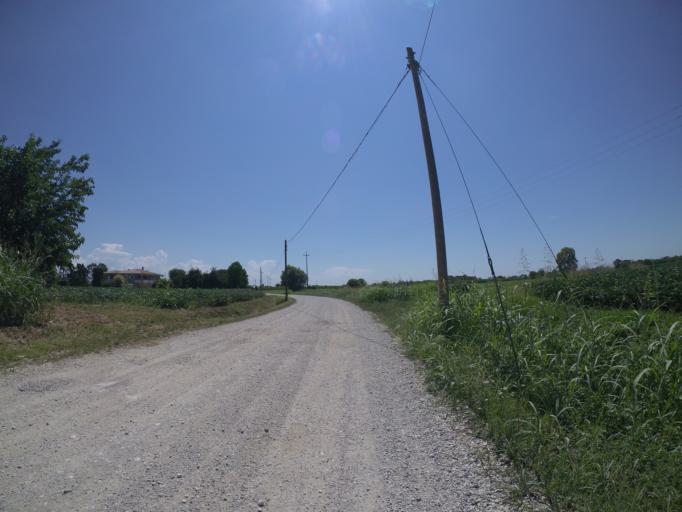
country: IT
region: Friuli Venezia Giulia
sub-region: Provincia di Udine
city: Talmassons
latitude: 45.9308
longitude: 13.0980
